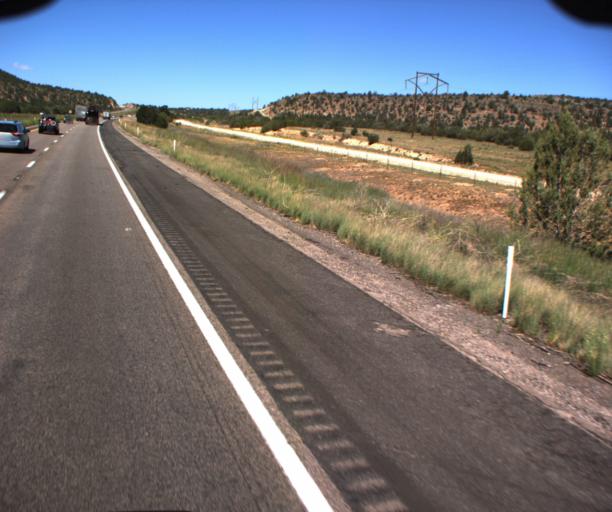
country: US
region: Arizona
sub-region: Mohave County
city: Peach Springs
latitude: 35.3031
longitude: -113.0027
